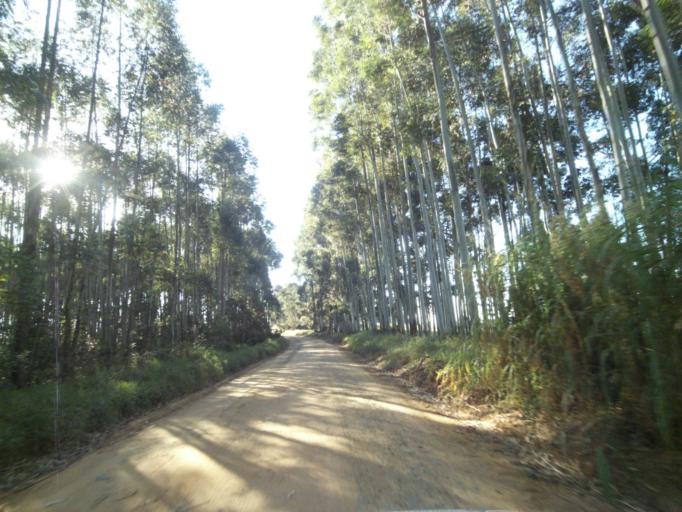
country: BR
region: Parana
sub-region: Tibagi
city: Tibagi
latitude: -24.5418
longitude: -50.6240
